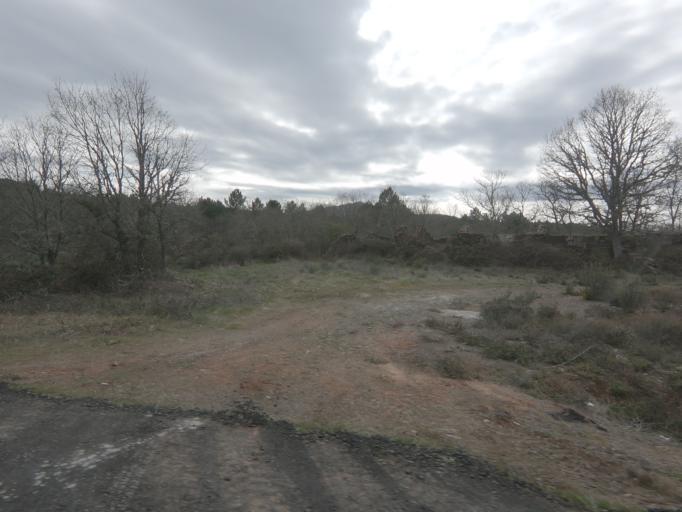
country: ES
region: Extremadura
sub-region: Provincia de Caceres
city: Acebo
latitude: 40.2542
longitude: -6.6883
